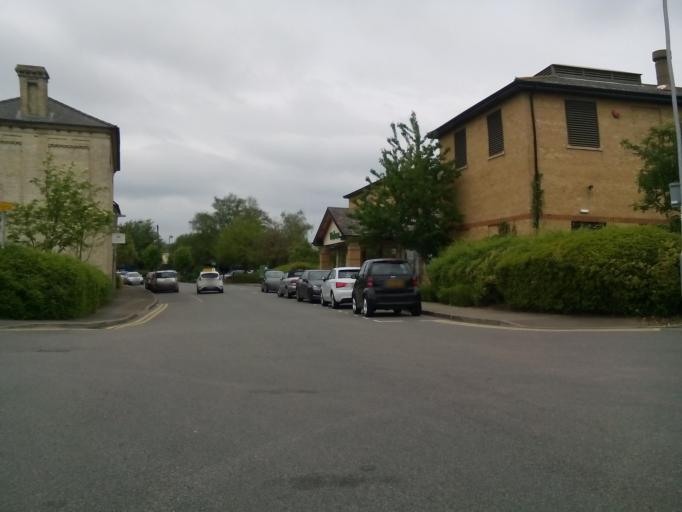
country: GB
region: England
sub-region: Cambridgeshire
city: Hemingford Grey
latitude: 52.3218
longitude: -0.0687
